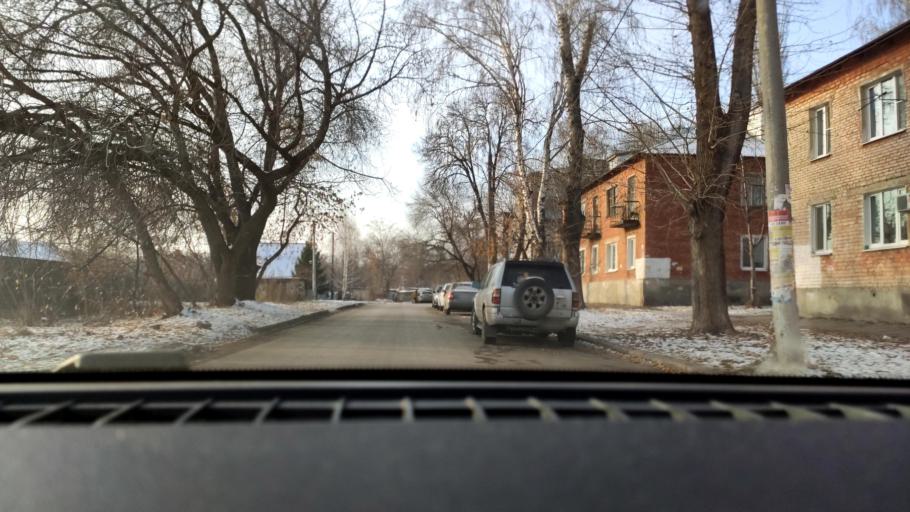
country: RU
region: Samara
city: Petra-Dubrava
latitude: 53.3009
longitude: 50.2733
